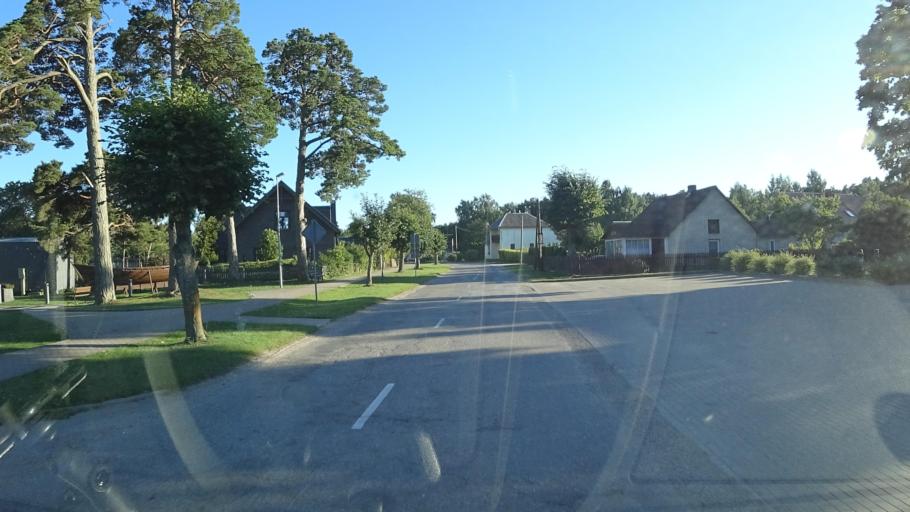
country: LV
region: Dundaga
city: Dundaga
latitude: 57.7425
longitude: 22.5846
